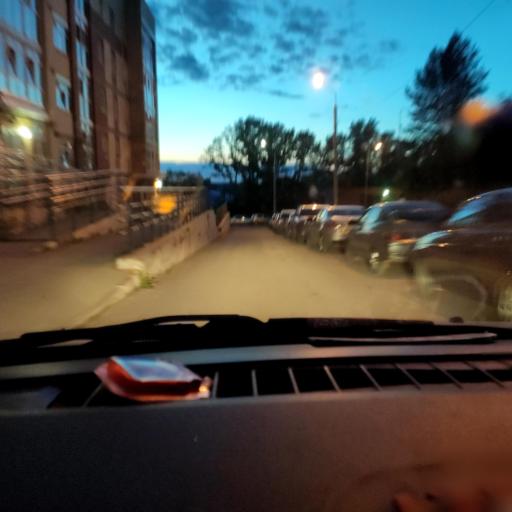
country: RU
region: Perm
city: Lobanovo
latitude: 57.8600
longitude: 56.2895
